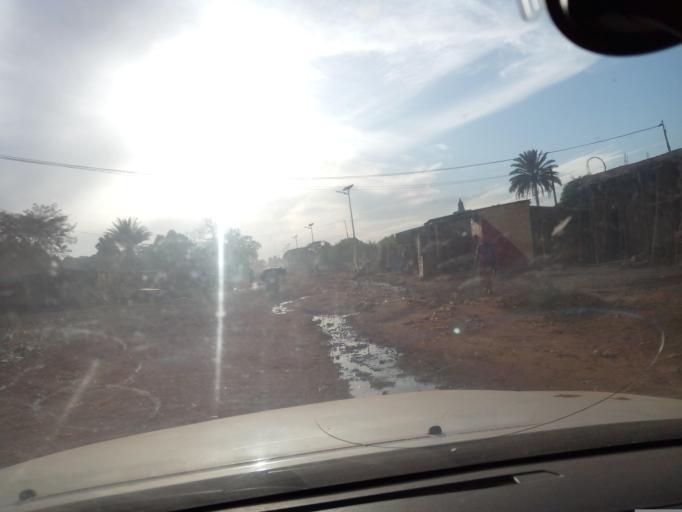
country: ML
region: Sikasso
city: Sikasso
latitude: 11.3131
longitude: -5.6499
